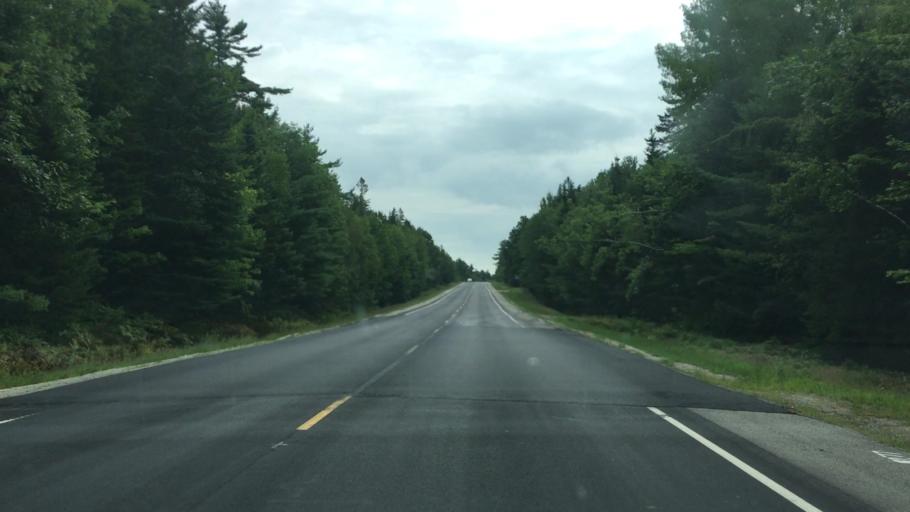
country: US
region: Maine
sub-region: Washington County
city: Addison
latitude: 44.9076
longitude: -67.8377
